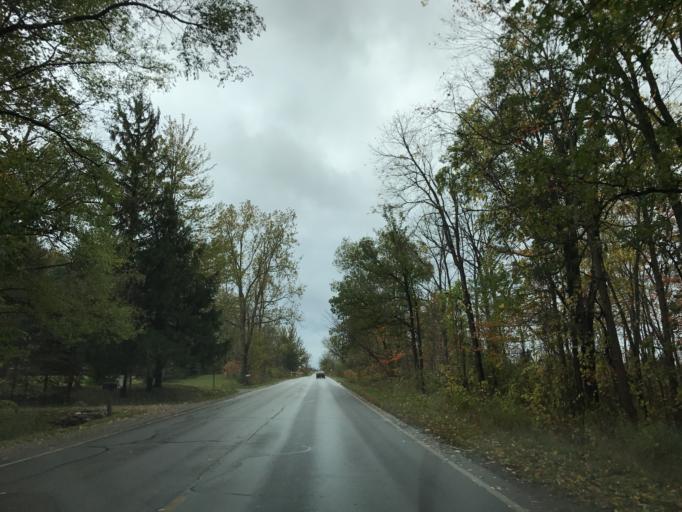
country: US
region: Michigan
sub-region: Oakland County
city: South Lyon
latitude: 42.4089
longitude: -83.6461
